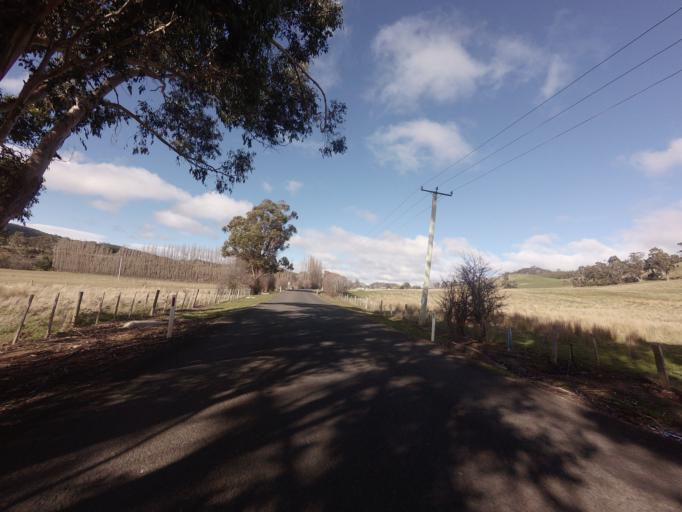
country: AU
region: Tasmania
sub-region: Derwent Valley
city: New Norfolk
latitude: -42.6100
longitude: 146.7086
